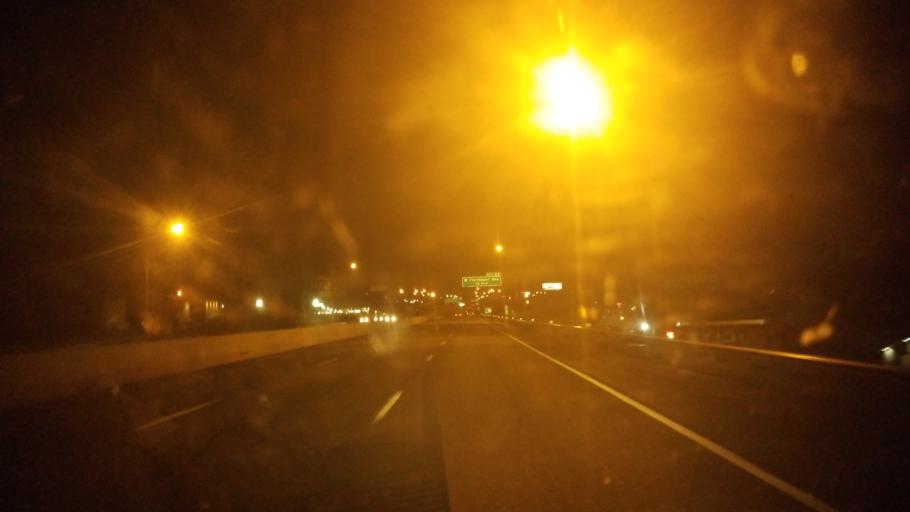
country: US
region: Missouri
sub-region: Saint Louis County
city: Black Jack
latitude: 38.7712
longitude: -90.2682
